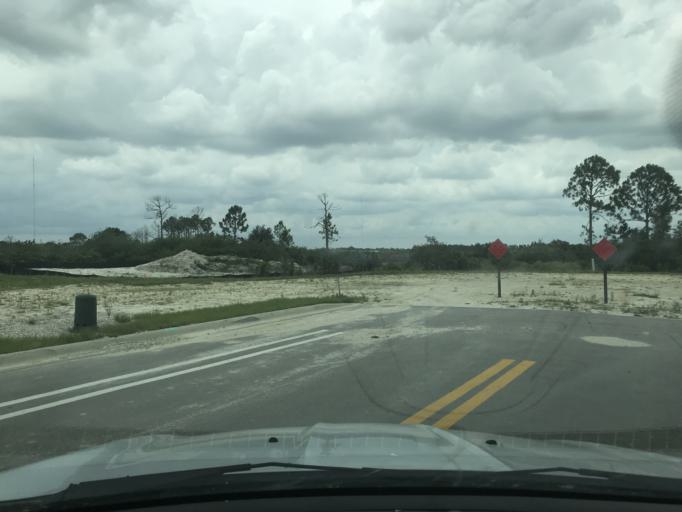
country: US
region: Florida
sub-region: Lee County
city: Olga
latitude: 26.7931
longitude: -81.7346
